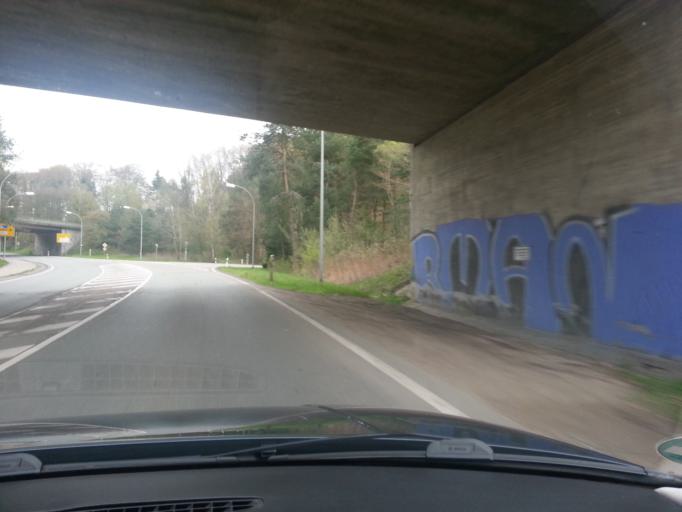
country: DE
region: Saarland
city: Sulzbach
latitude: 49.2622
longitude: 7.0513
